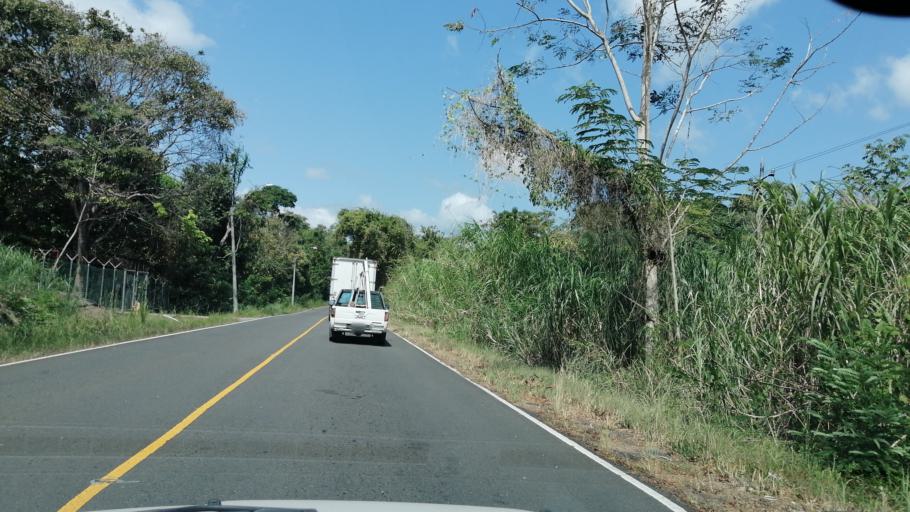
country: PA
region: Panama
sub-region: Distrito de Panama
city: Ancon
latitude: 8.9291
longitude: -79.5730
